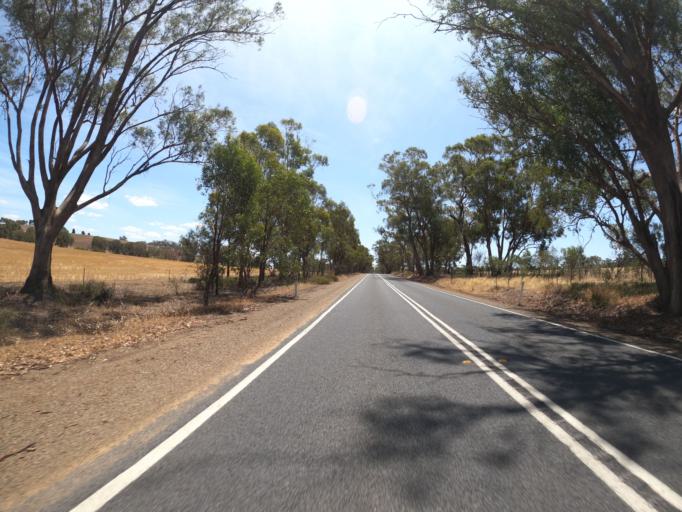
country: AU
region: Victoria
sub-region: Benalla
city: Benalla
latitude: -36.3740
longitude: 145.9738
